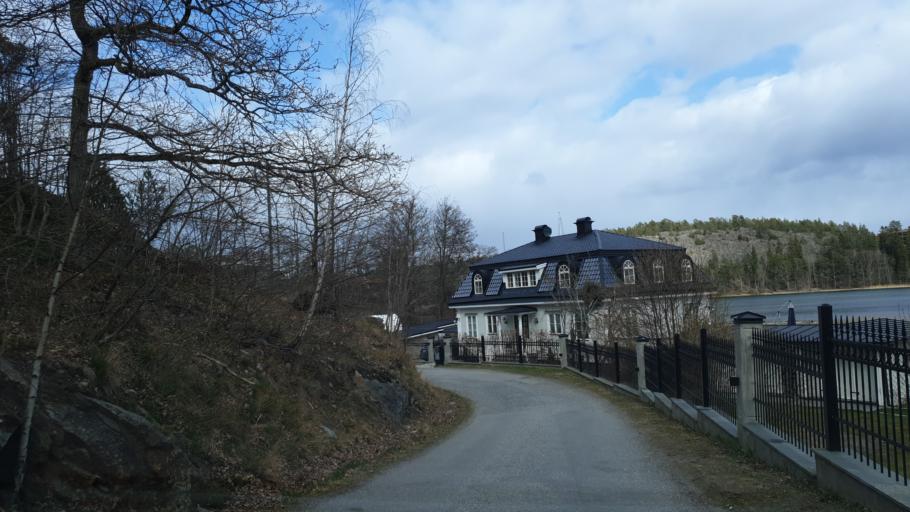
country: SE
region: Stockholm
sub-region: Nacka Kommun
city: Boo
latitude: 59.3245
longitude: 18.3109
